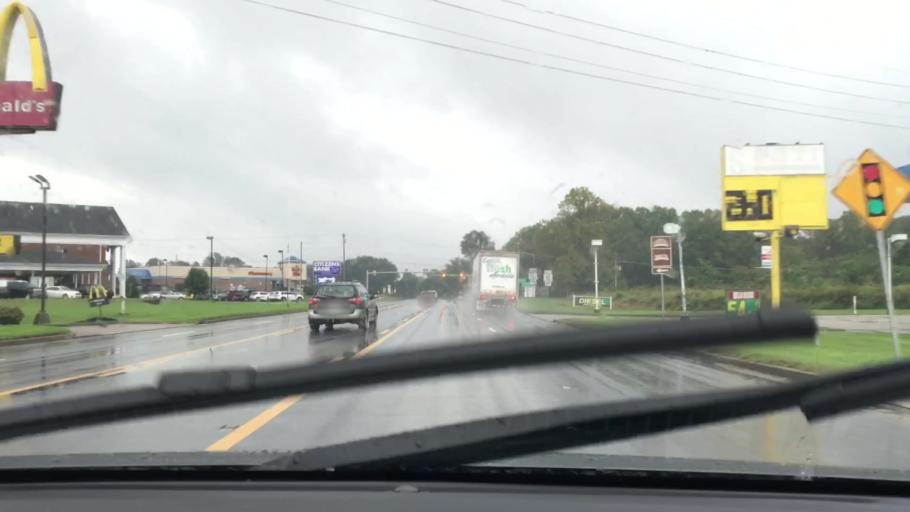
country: US
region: Tennessee
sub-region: Macon County
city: Lafayette
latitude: 36.5202
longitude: -86.0360
